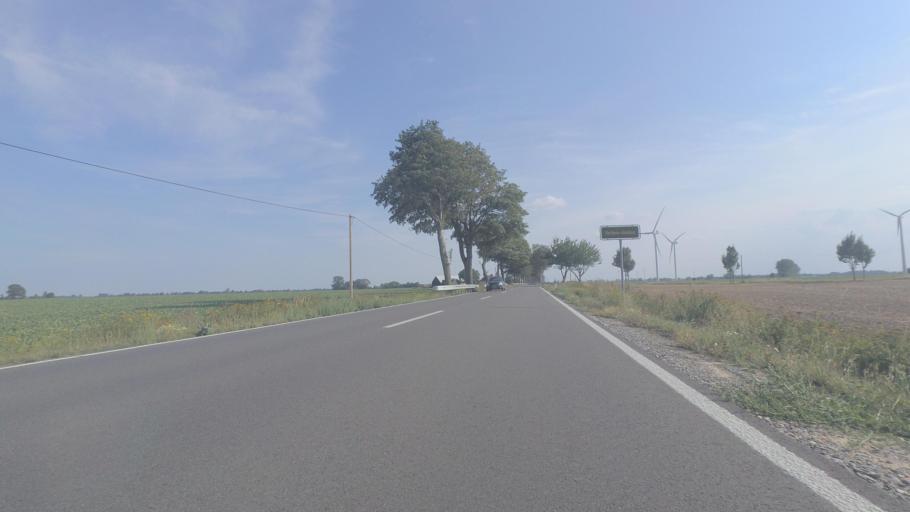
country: DE
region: Mecklenburg-Vorpommern
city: Gormin
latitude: 54.0168
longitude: 13.1388
